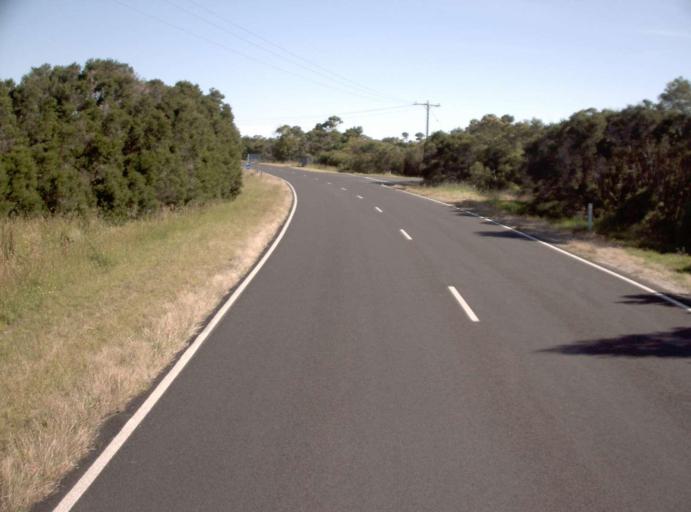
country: AU
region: Victoria
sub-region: Latrobe
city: Traralgon
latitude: -38.6411
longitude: 146.6713
